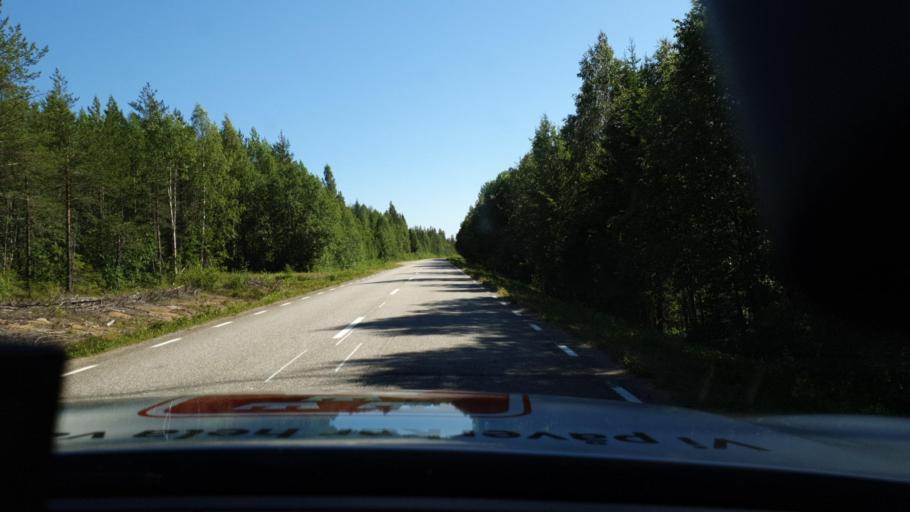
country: SE
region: Norrbotten
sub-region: Lulea Kommun
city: Ranea
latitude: 66.0314
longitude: 22.2958
